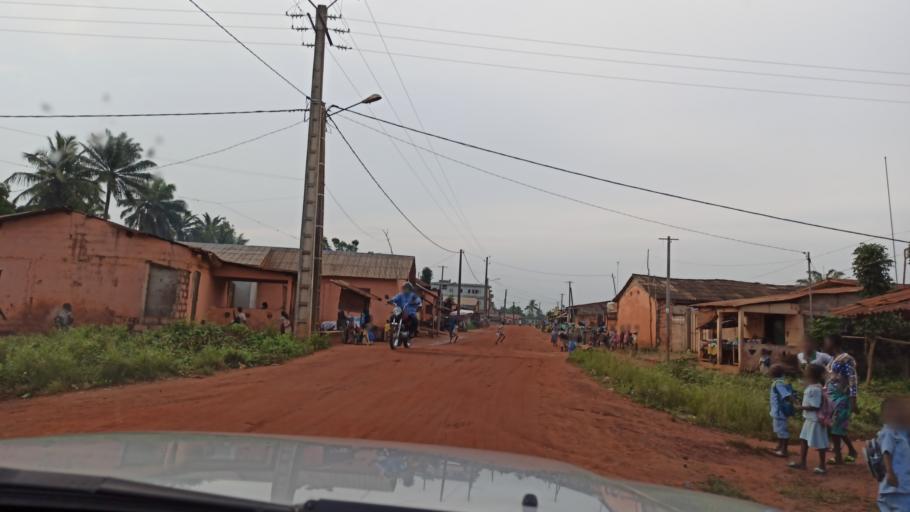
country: BJ
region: Queme
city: Porto-Novo
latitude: 6.5215
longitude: 2.6740
